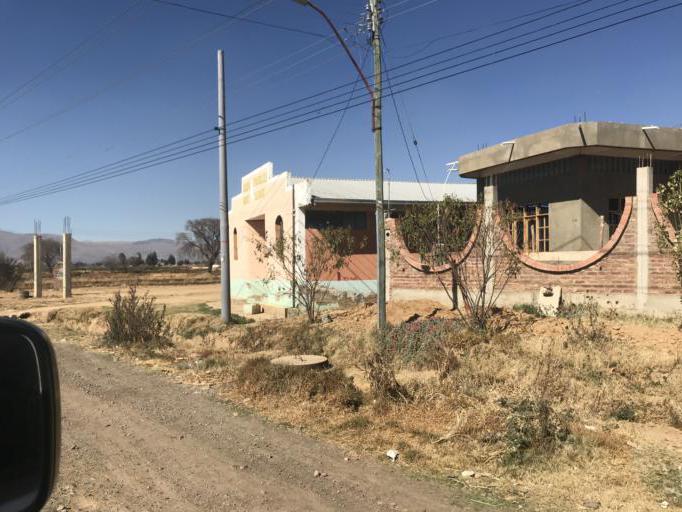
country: BO
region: Cochabamba
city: Cliza
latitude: -17.5718
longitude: -65.8982
